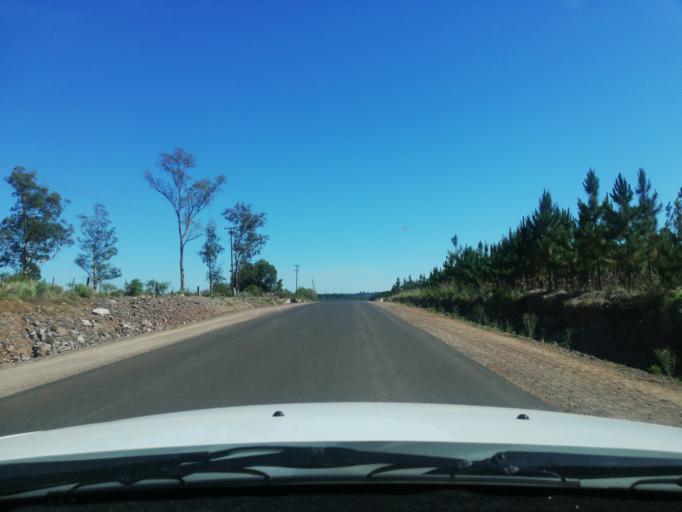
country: AR
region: Misiones
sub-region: Departamento de Candelaria
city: Candelaria
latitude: -27.5015
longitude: -55.7369
